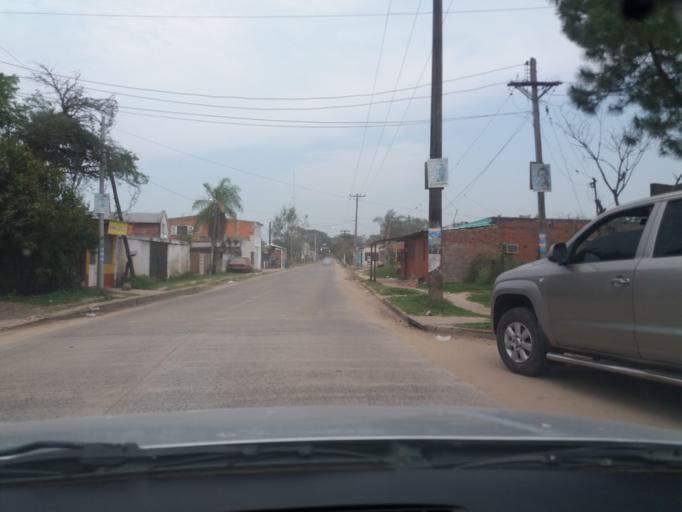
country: AR
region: Corrientes
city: Corrientes
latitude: -27.5123
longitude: -58.8024
